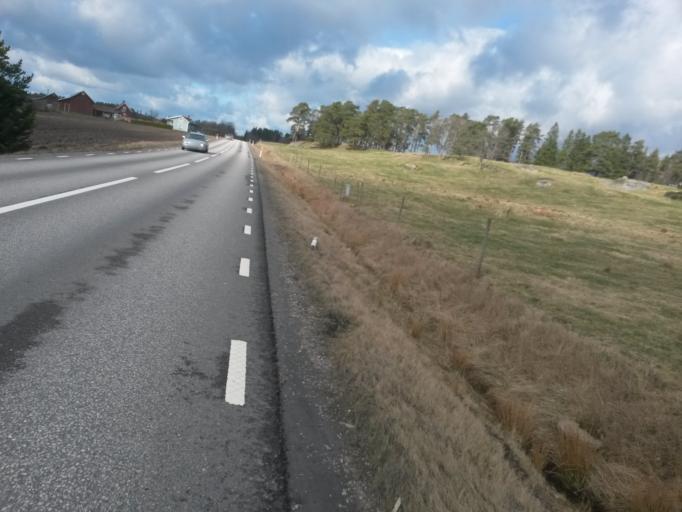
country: SE
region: Vaestra Goetaland
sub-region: Vargarda Kommun
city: Vargarda
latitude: 58.0513
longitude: 12.7725
